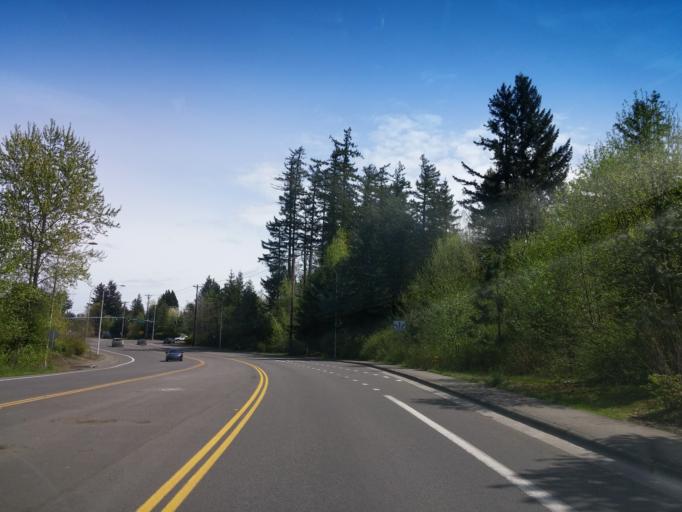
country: US
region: Oregon
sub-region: Washington County
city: Cedar Mill
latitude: 45.5268
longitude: -122.7950
